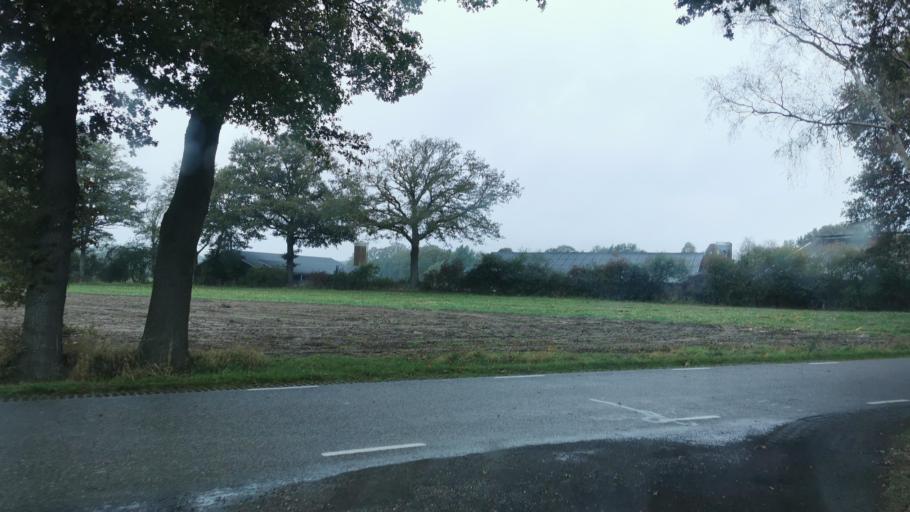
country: NL
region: Overijssel
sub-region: Gemeente Losser
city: Losser
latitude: 52.3050
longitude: 7.0166
